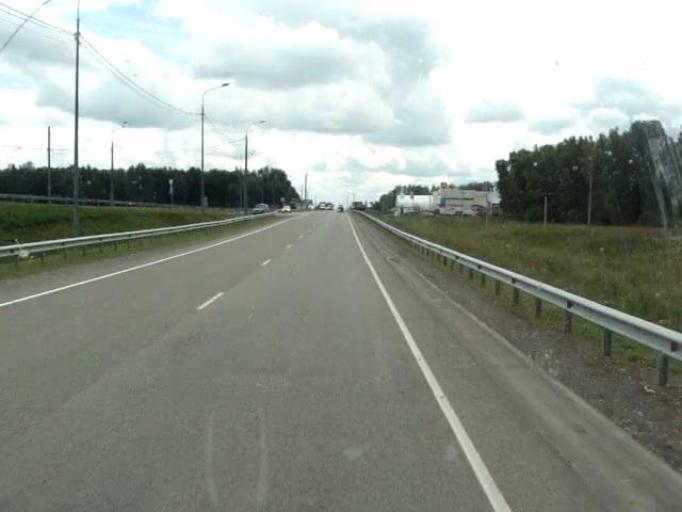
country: RU
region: Altai Krai
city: Zarya
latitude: 52.5776
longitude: 85.1783
